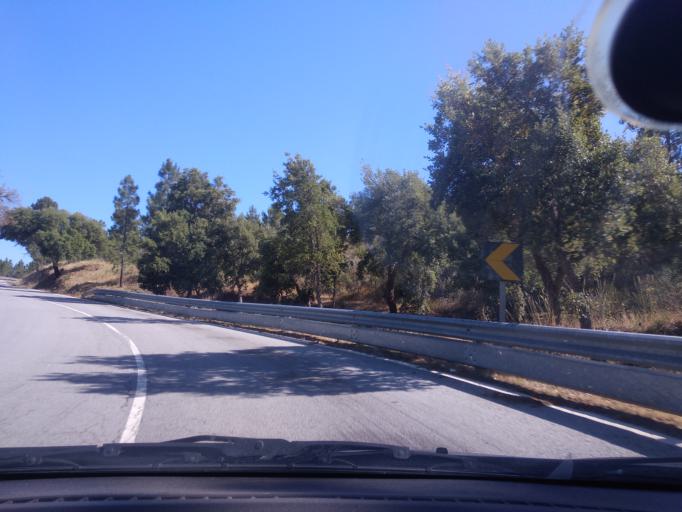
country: PT
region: Portalegre
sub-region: Nisa
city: Nisa
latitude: 39.6014
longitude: -7.6596
